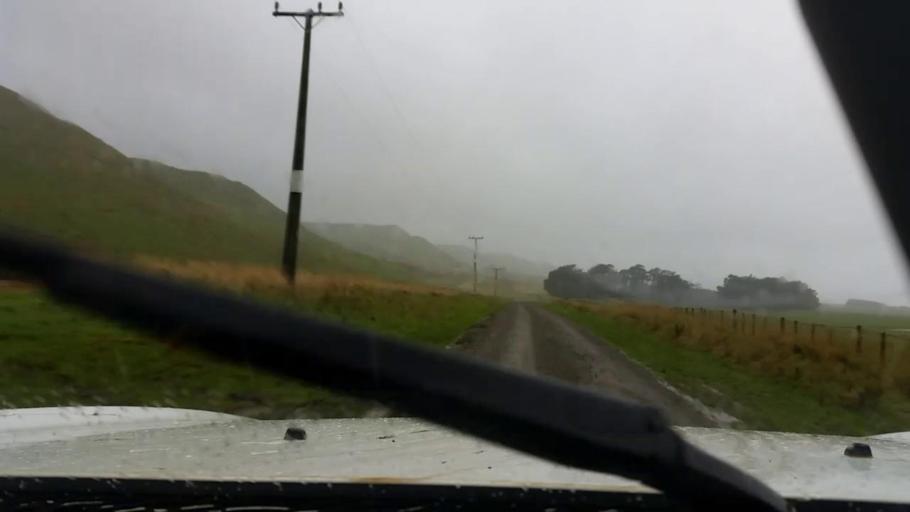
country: NZ
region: Wellington
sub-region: Masterton District
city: Masterton
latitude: -41.2554
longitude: 175.9077
